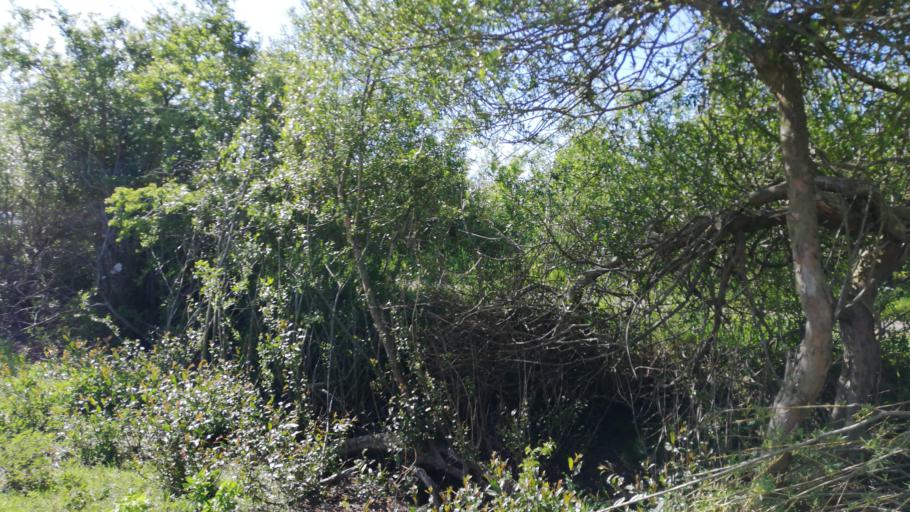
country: DE
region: Schleswig-Holstein
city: Borgsum
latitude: 54.7027
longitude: 8.4596
